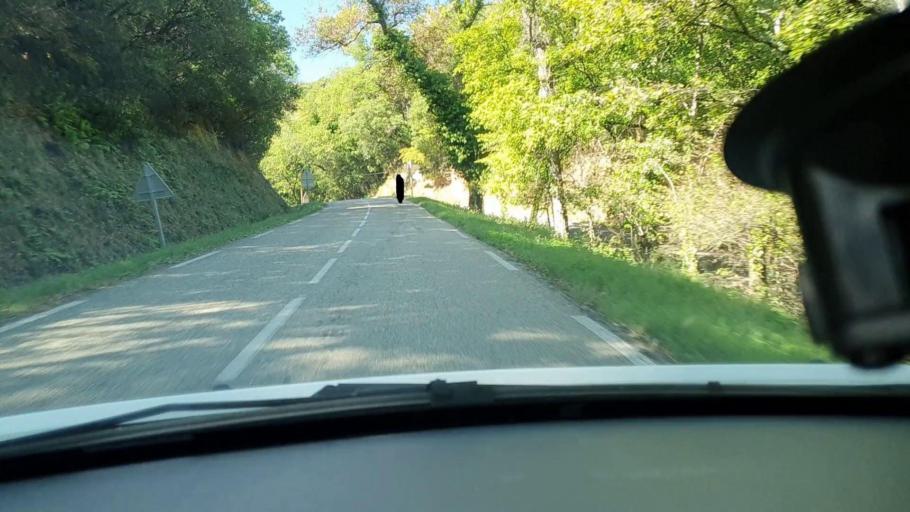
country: FR
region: Languedoc-Roussillon
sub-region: Departement du Gard
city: Saint-Julien-de-Peyrolas
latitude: 44.2373
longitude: 4.5485
